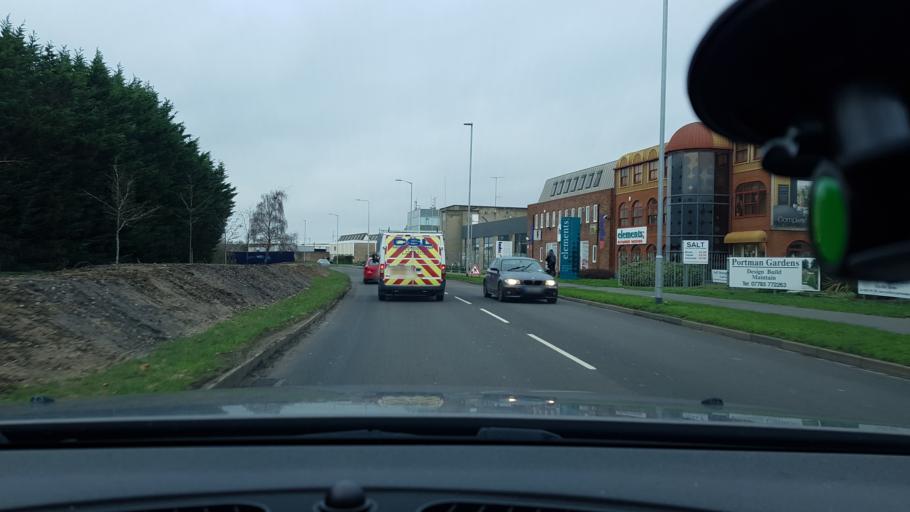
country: GB
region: England
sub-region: Reading
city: Reading
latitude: 51.4592
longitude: -0.9920
